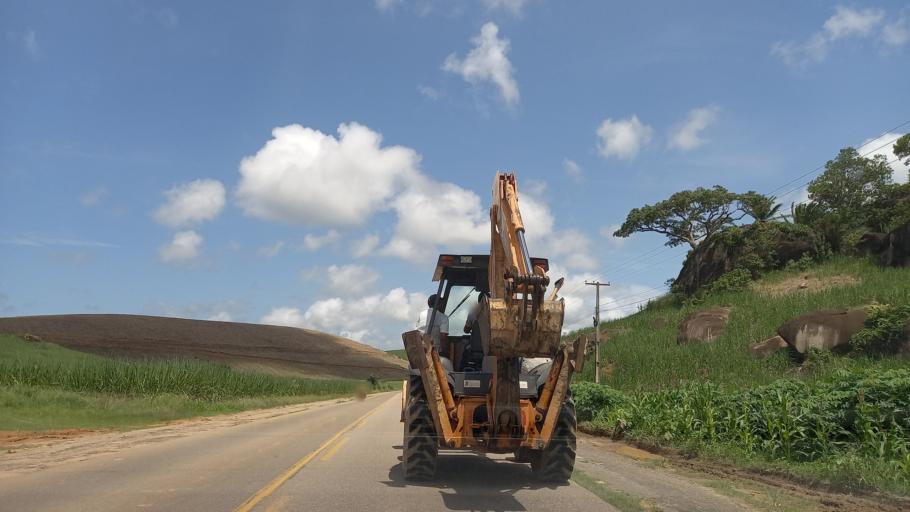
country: BR
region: Pernambuco
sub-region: Sirinhaem
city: Sirinhaem
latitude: -8.6041
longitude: -35.1165
